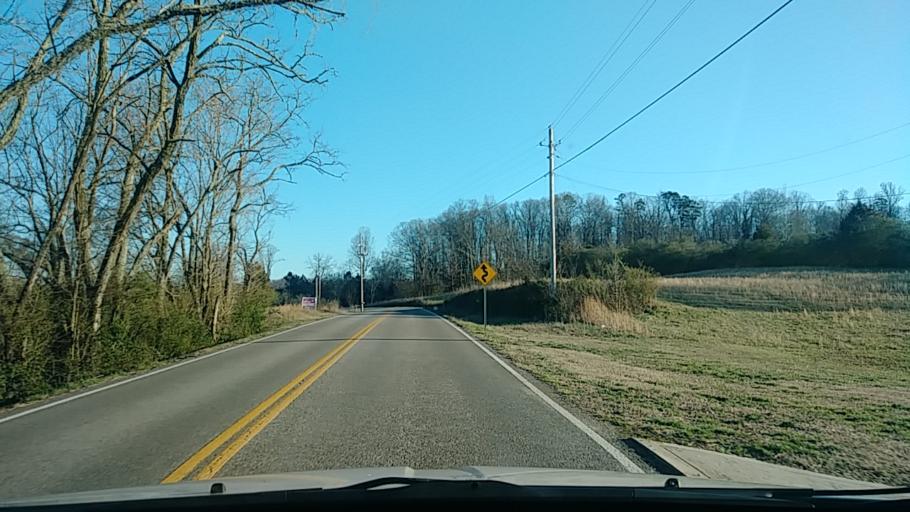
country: US
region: Tennessee
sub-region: Hamblen County
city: Morristown
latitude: 36.2004
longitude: -83.4015
